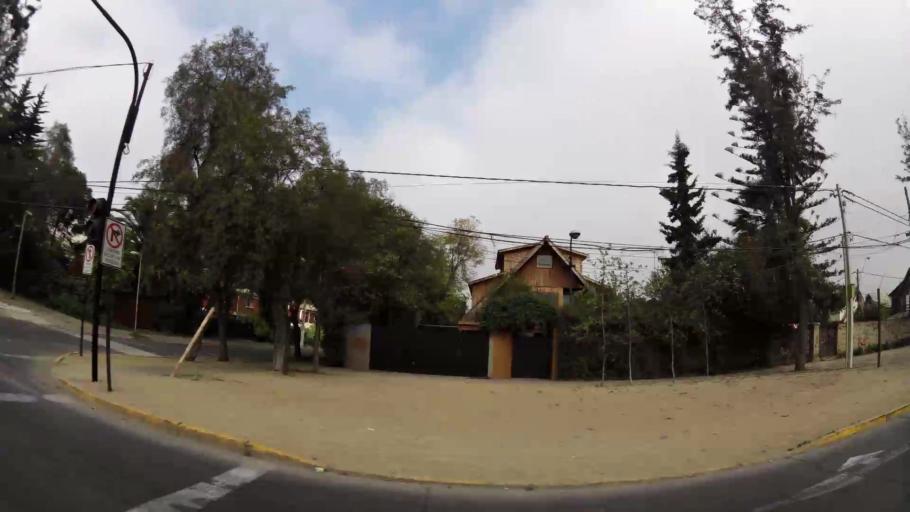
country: CL
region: Santiago Metropolitan
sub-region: Provincia de Santiago
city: Villa Presidente Frei, Nunoa, Santiago, Chile
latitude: -33.4131
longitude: -70.5407
